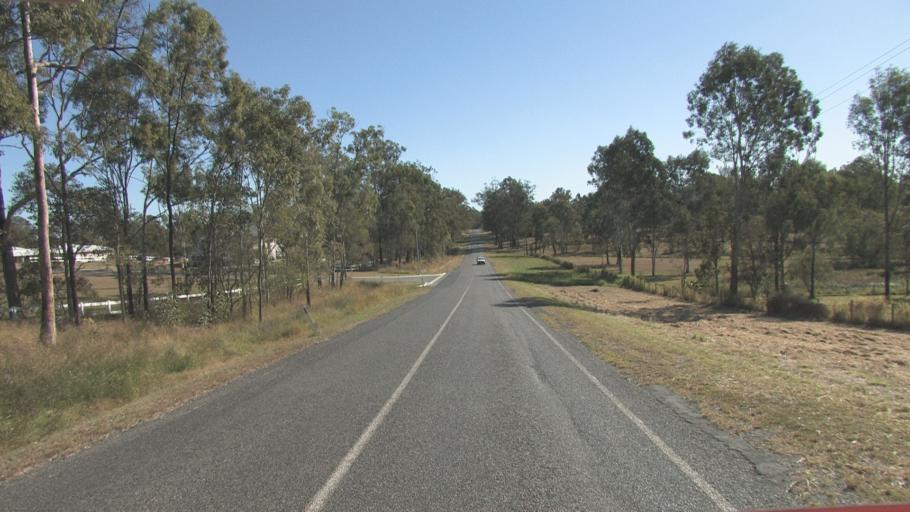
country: AU
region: Queensland
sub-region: Logan
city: North Maclean
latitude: -27.7923
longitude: 153.0241
